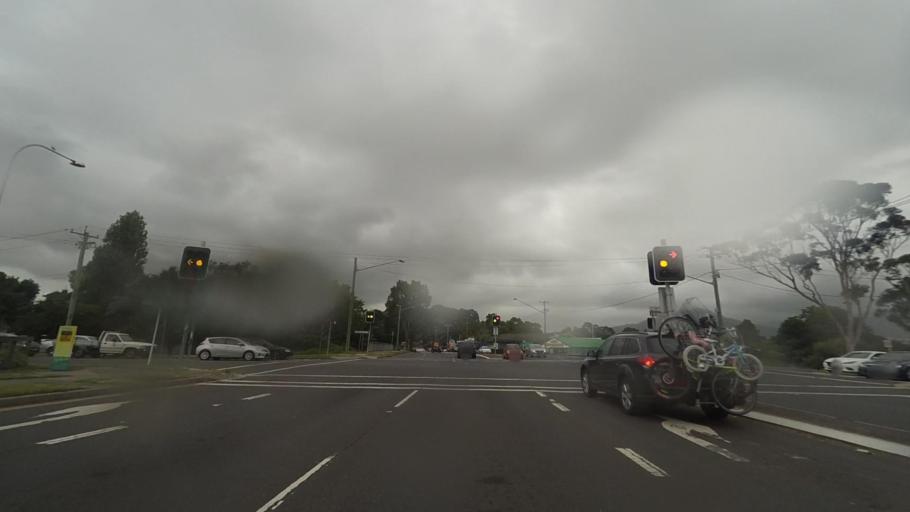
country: AU
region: New South Wales
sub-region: Wollongong
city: Mangerton
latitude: -34.4388
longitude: 150.8583
